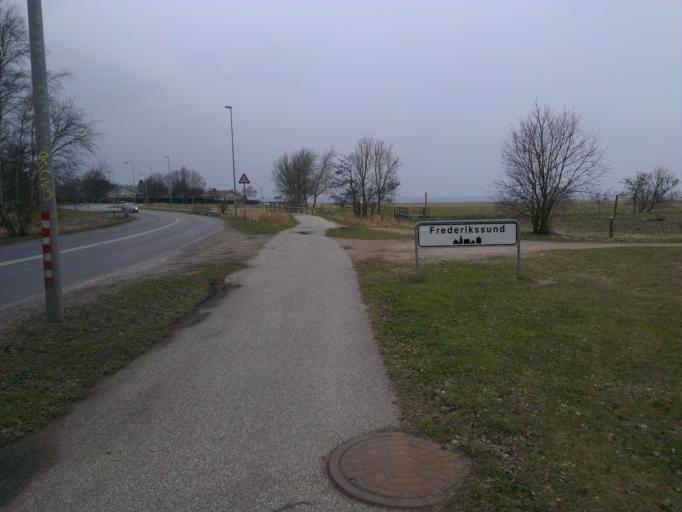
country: DK
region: Capital Region
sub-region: Frederikssund Kommune
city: Frederikssund
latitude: 55.8562
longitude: 12.0678
